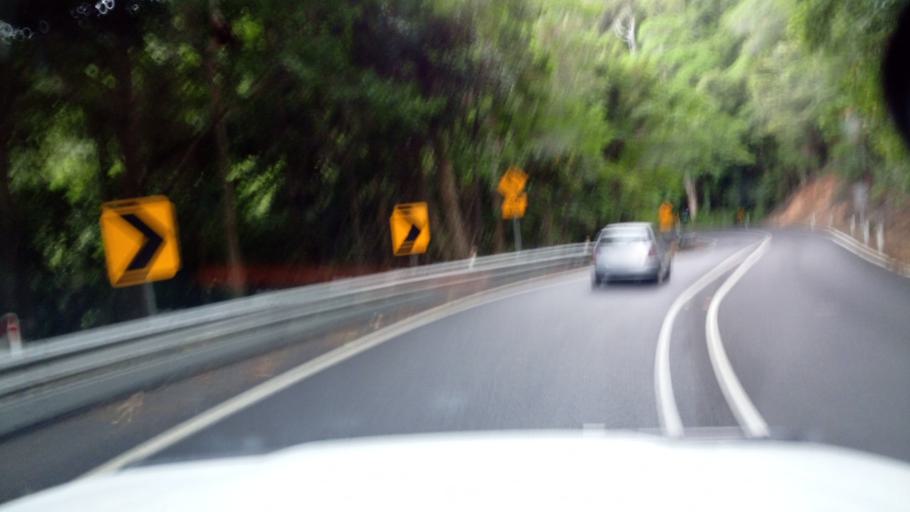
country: AU
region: Queensland
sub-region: Tablelands
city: Kuranda
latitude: -16.8449
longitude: 145.6736
